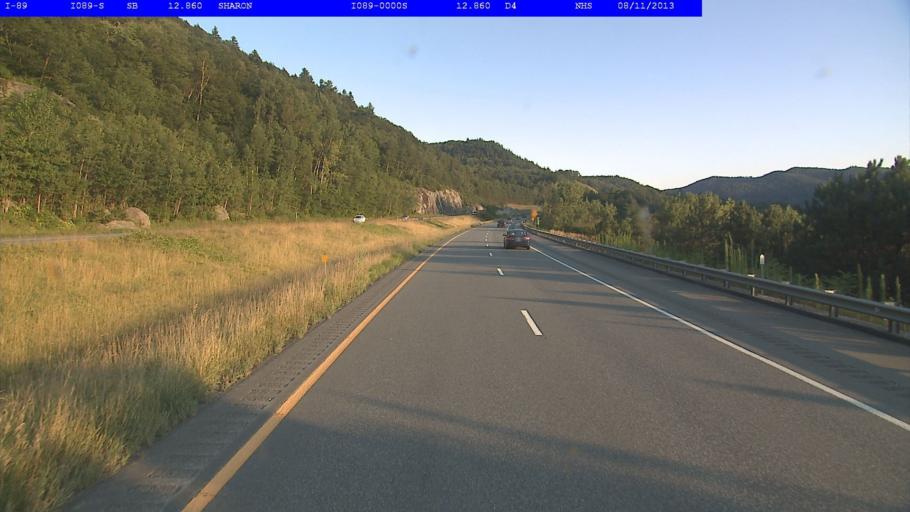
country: US
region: Vermont
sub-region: Windsor County
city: Woodstock
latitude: 43.7805
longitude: -72.4455
